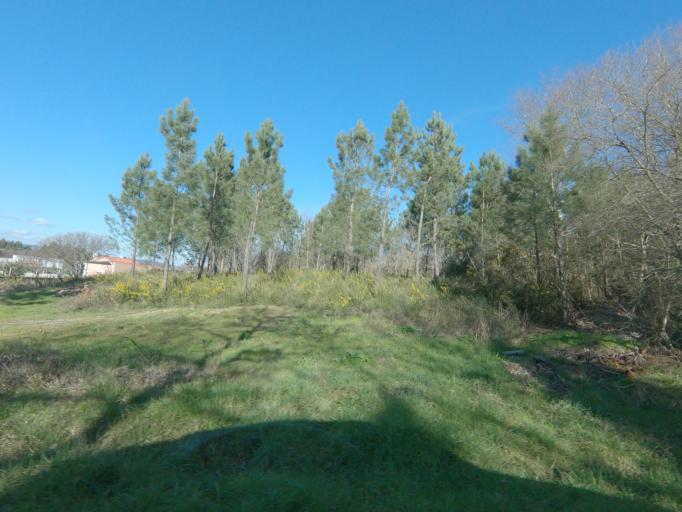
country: ES
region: Galicia
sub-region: Provincia da Coruna
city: Ribeira
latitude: 42.7177
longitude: -8.4412
